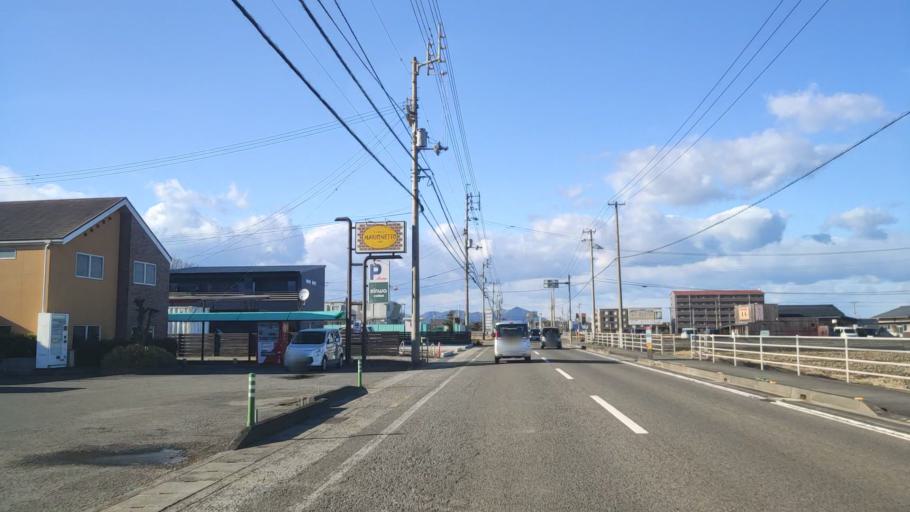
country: JP
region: Ehime
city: Saijo
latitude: 33.9121
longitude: 133.1093
